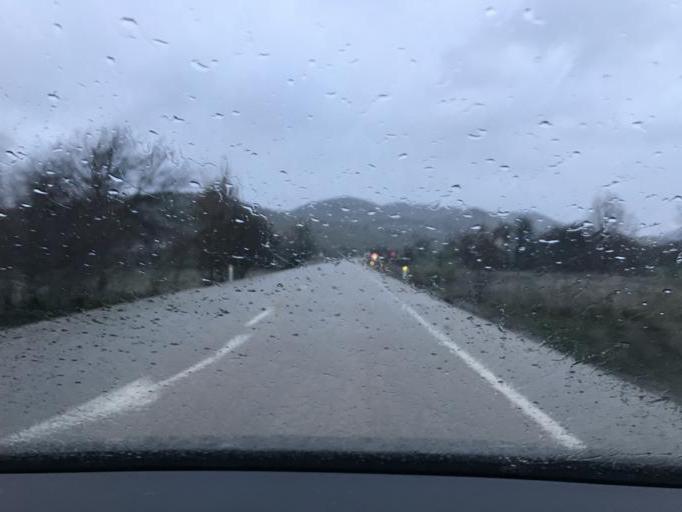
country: ES
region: Andalusia
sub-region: Provincia de Granada
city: Campotejar
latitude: 37.4504
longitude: -3.6392
